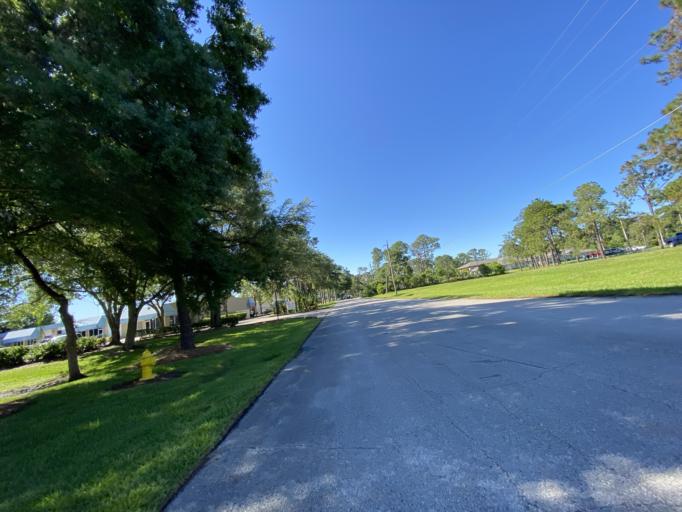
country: US
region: Florida
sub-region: Volusia County
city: Port Orange
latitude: 29.1528
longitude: -80.9947
